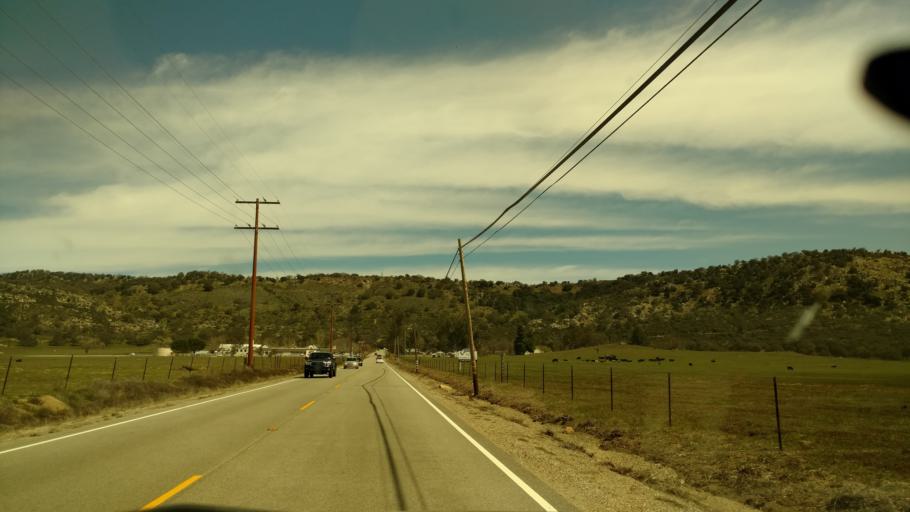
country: US
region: California
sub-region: San Diego County
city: Julian
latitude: 33.1073
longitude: -116.6803
